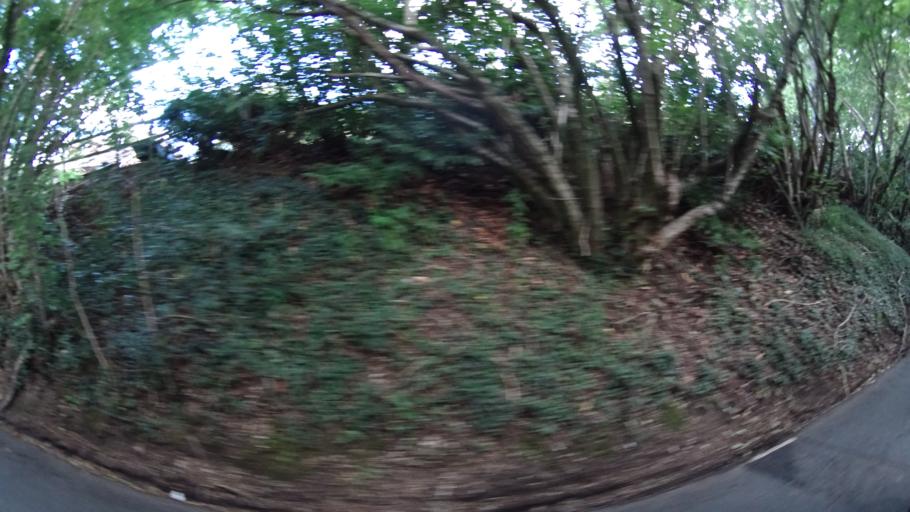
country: GB
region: England
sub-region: Hampshire
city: Romsey
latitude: 51.0099
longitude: -1.5271
